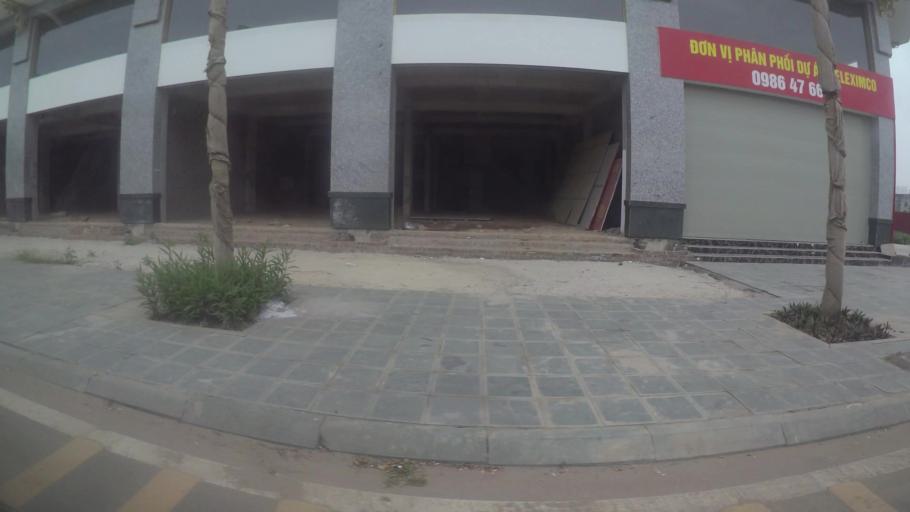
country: VN
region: Ha Noi
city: Ha Dong
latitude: 20.9841
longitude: 105.7407
